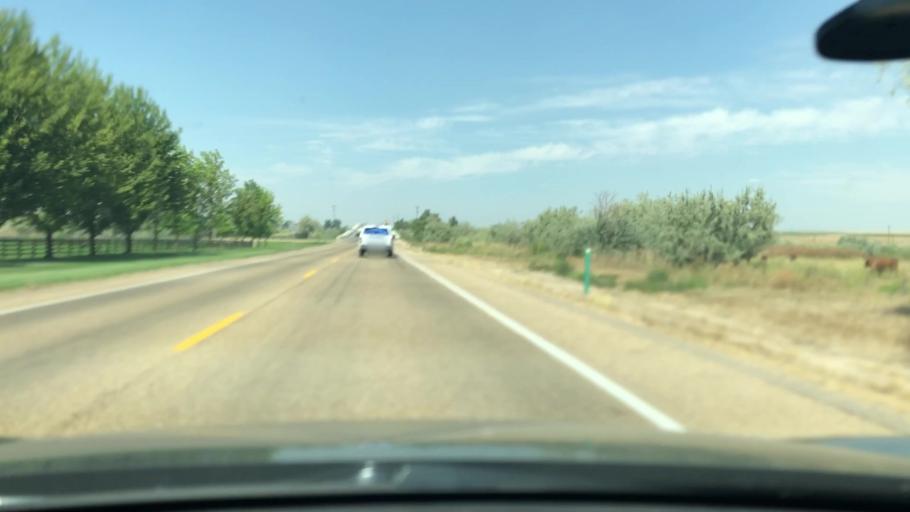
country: US
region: Idaho
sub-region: Canyon County
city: Parma
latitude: 43.7608
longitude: -116.9117
